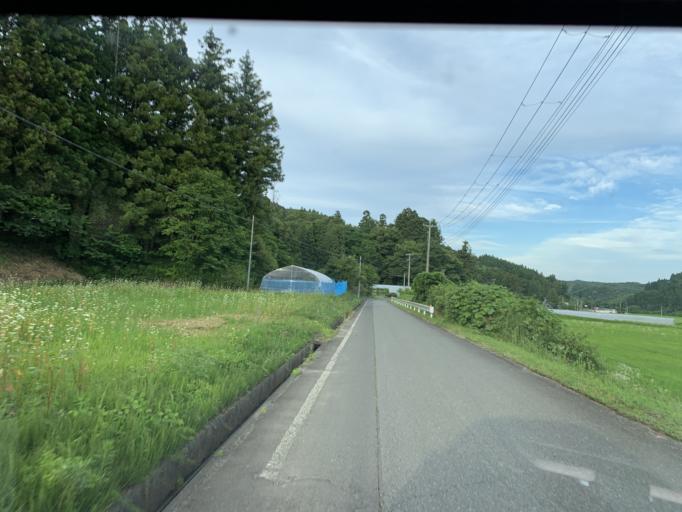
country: JP
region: Iwate
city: Ichinoseki
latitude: 38.9133
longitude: 141.0484
